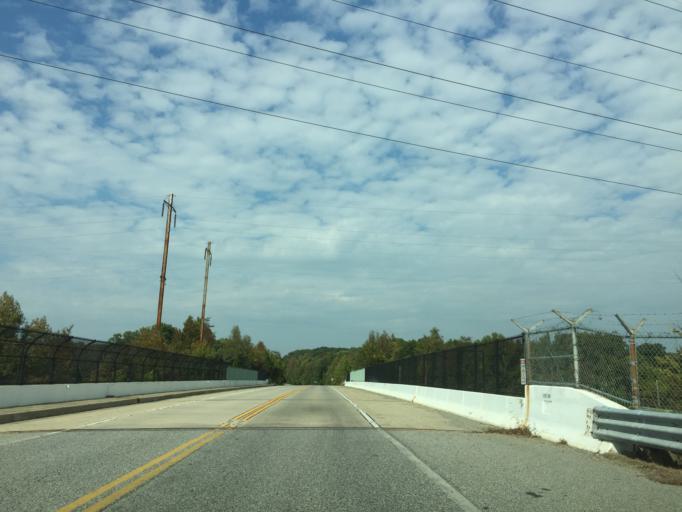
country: US
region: Maryland
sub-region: Harford County
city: Edgewood
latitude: 39.4111
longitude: -76.3020
